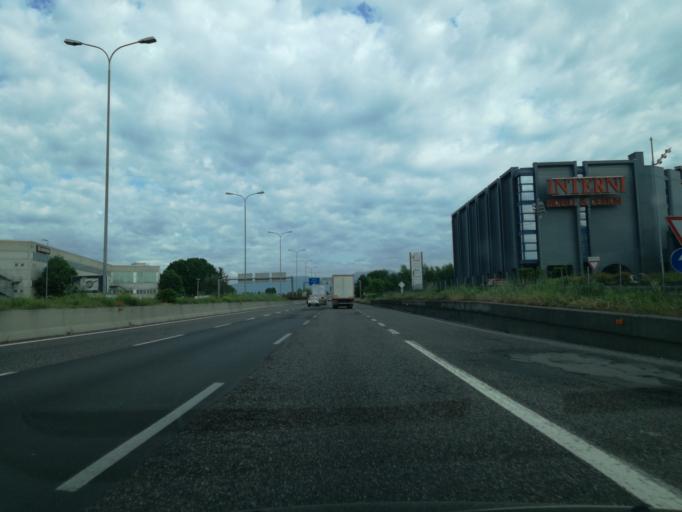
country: IT
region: Lombardy
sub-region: Provincia di Monza e Brianza
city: Verano Brianza
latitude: 45.6799
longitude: 9.2177
